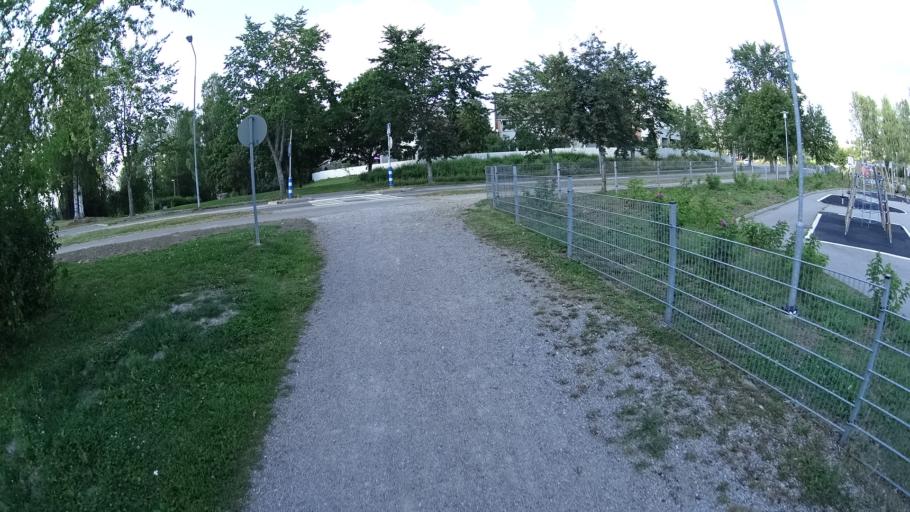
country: FI
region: Uusimaa
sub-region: Porvoo
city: Porvoo
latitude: 60.4091
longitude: 25.6631
